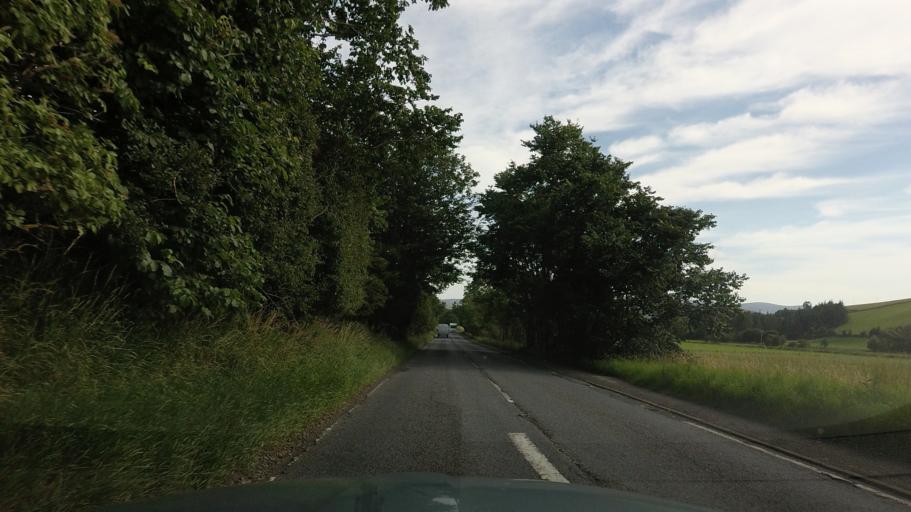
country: GB
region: Scotland
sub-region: The Scottish Borders
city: Peebles
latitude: 55.6728
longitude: -3.2013
